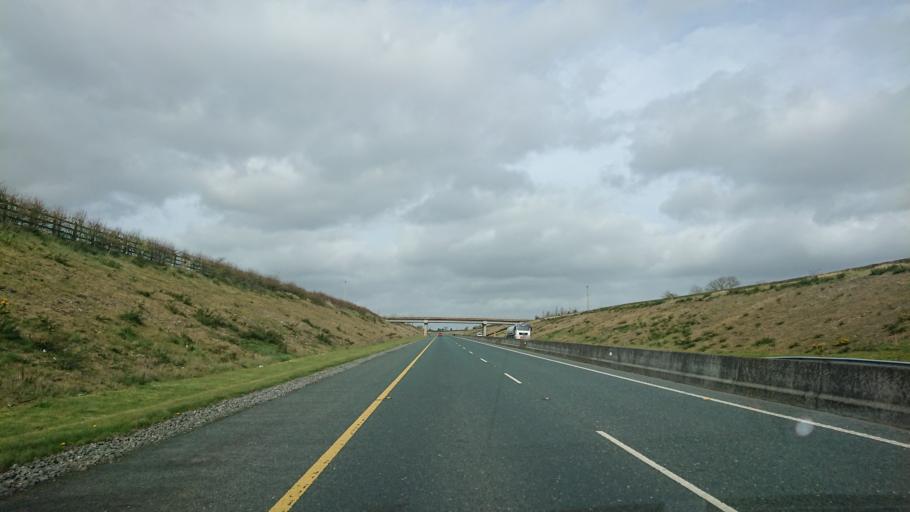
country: IE
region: Leinster
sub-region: County Carlow
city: Carlow
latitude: 52.8147
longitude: -6.8518
